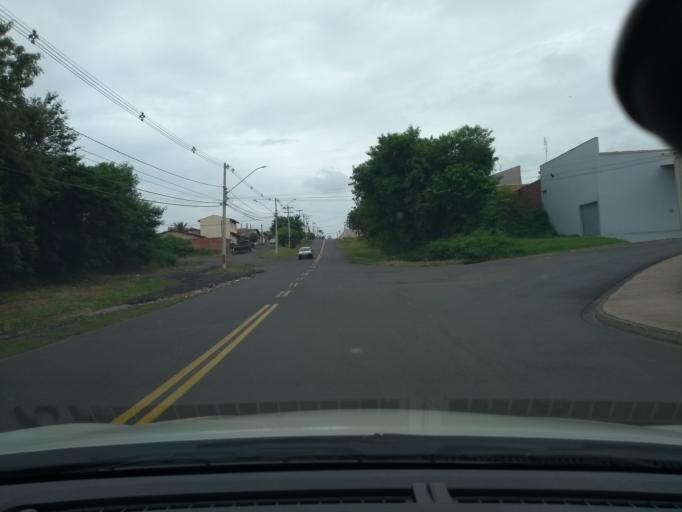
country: BR
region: Sao Paulo
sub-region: Rio Claro
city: Rio Claro
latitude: -22.3708
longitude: -47.5363
